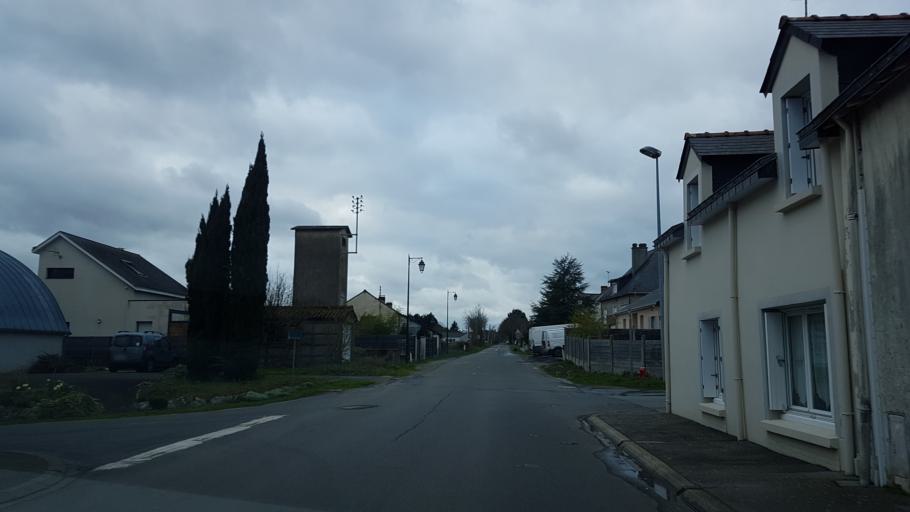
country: FR
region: Pays de la Loire
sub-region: Departement de la Loire-Atlantique
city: Le Gavre
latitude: 47.5221
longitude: -1.7517
